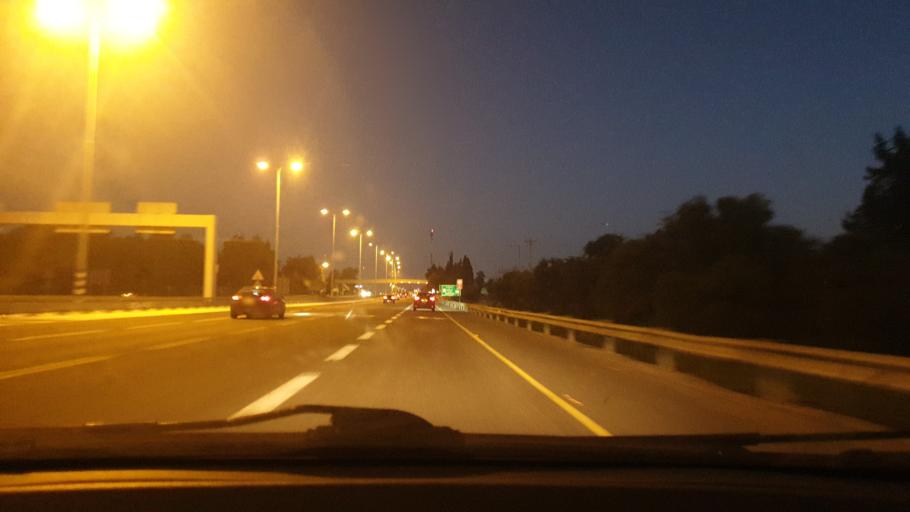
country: IL
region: Central District
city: Bet Dagan
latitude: 32.0080
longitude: 34.8158
